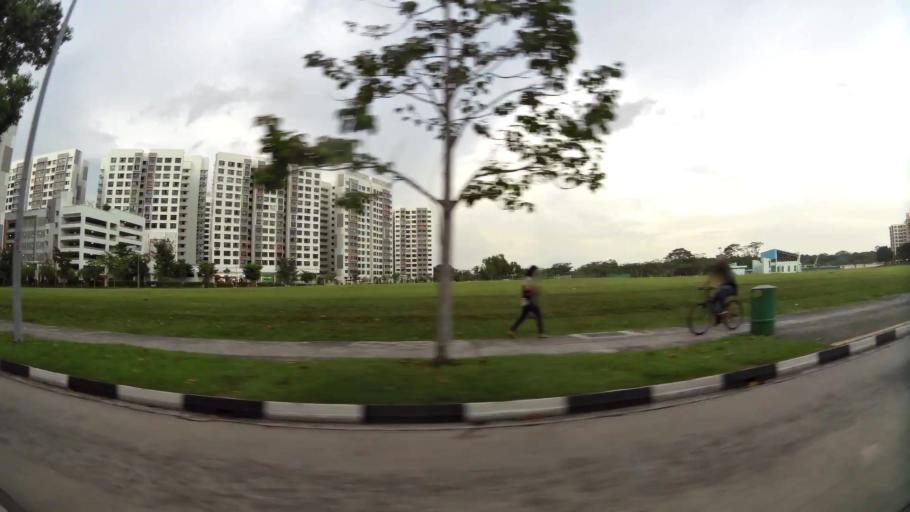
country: MY
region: Johor
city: Kampung Pasir Gudang Baru
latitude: 1.4303
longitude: 103.8453
